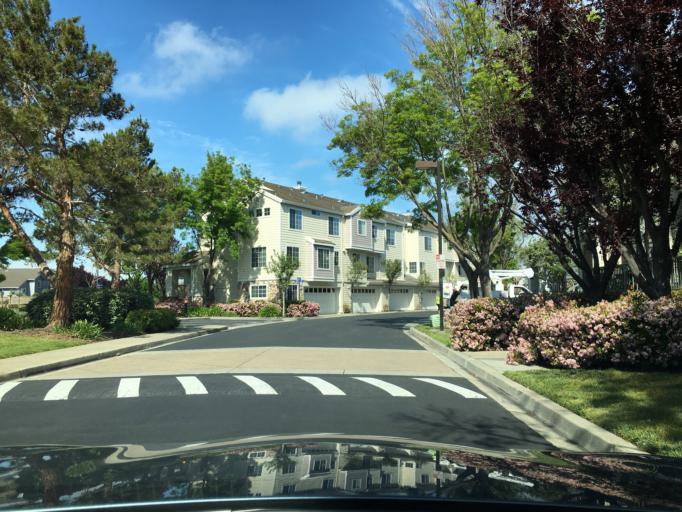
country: US
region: California
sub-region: San Mateo County
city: Redwood Shores
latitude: 37.5430
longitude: -122.2395
